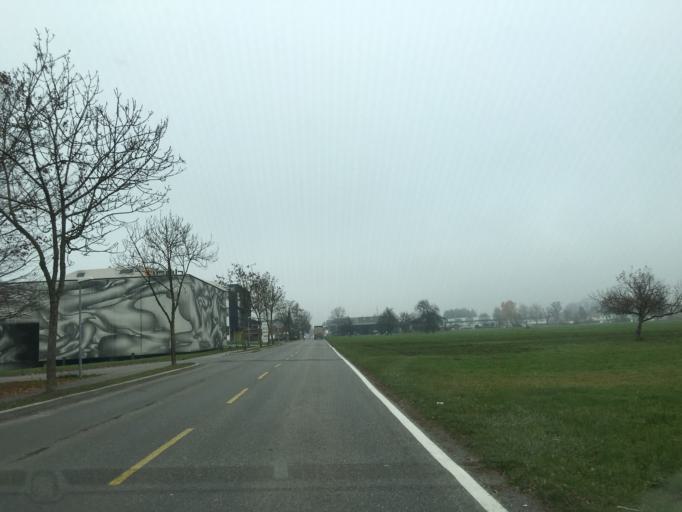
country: AT
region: Vorarlberg
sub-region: Politischer Bezirk Dornbirn
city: Lustenau
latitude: 47.4214
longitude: 9.6731
